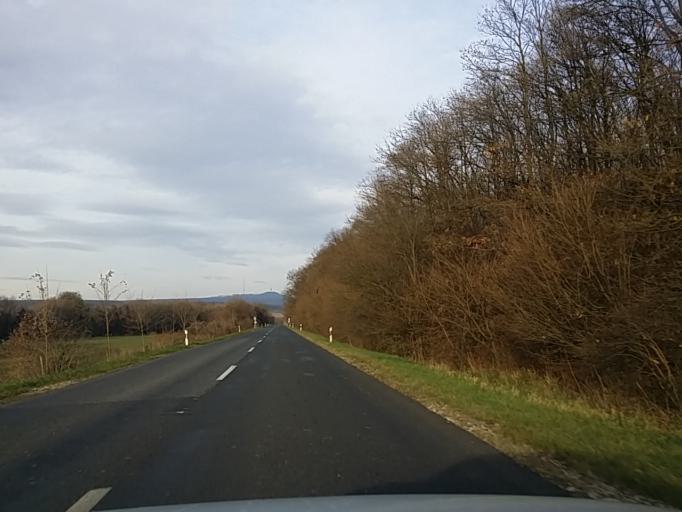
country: HU
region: Veszprem
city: Urkut
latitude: 46.9841
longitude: 17.6293
